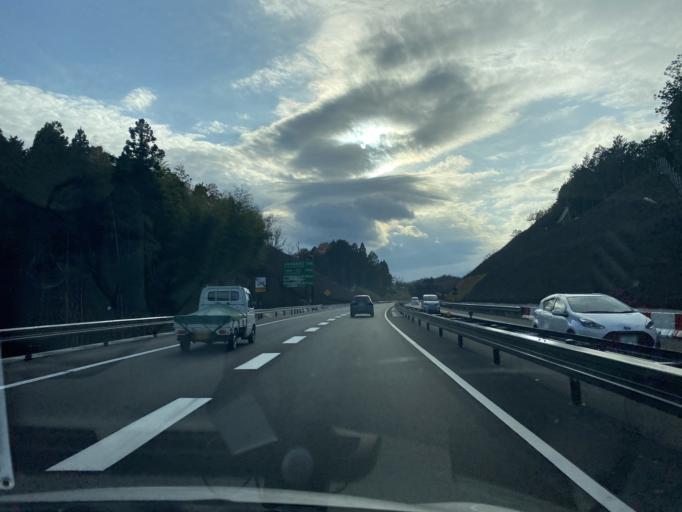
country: JP
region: Hyogo
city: Toyooka
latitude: 35.4904
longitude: 134.7805
